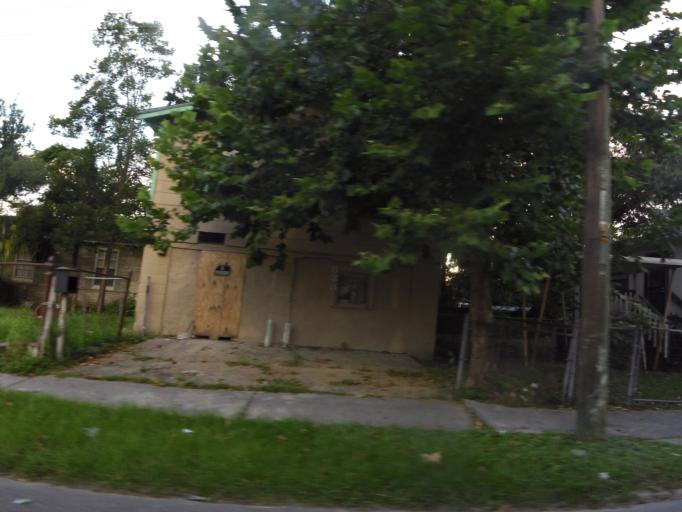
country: US
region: Florida
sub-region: Duval County
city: Jacksonville
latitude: 30.3381
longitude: -81.6815
